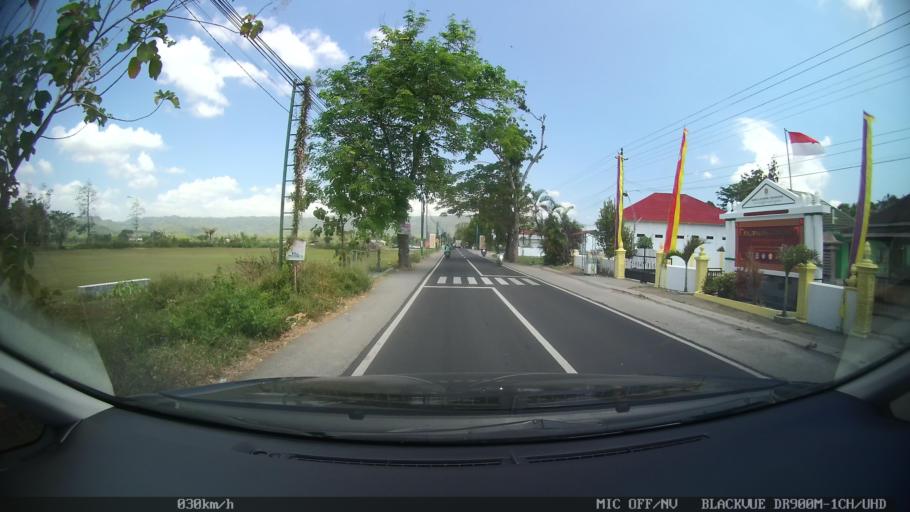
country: ID
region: Daerah Istimewa Yogyakarta
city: Pundong
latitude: -7.9267
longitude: 110.3735
